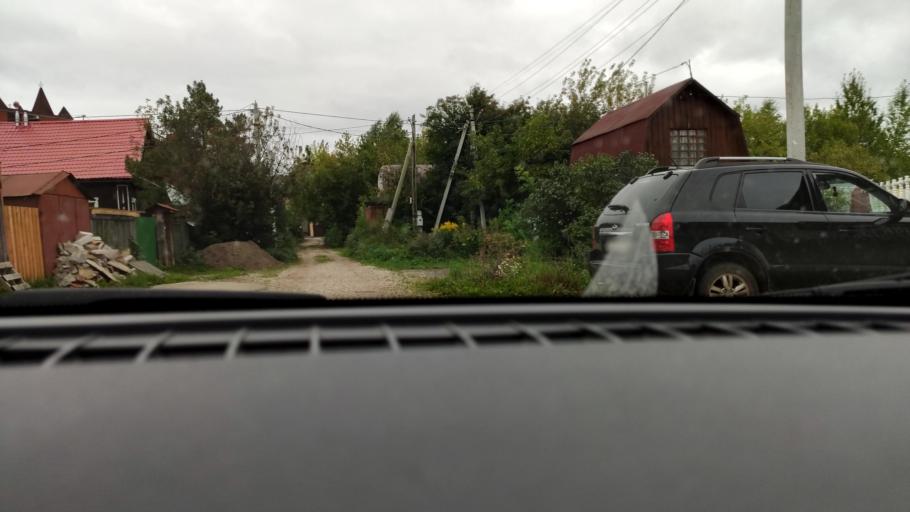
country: RU
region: Perm
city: Perm
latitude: 57.9926
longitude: 56.3099
